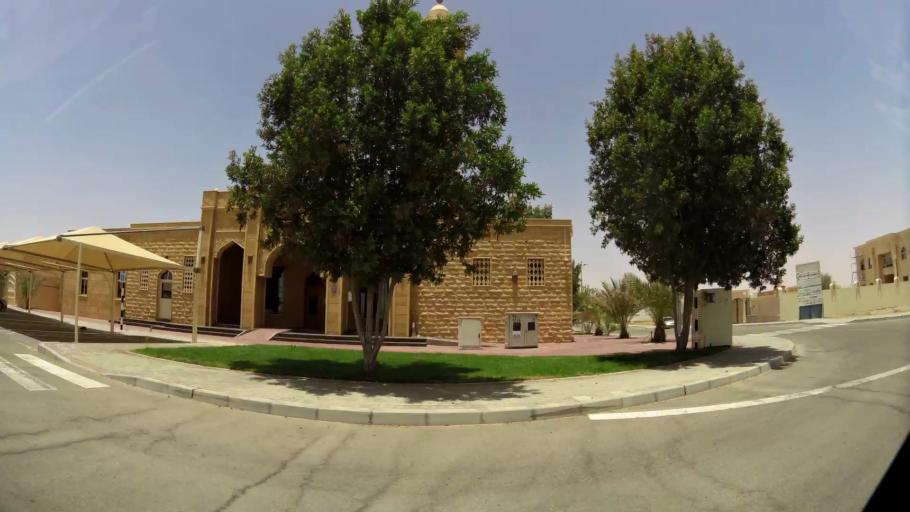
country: OM
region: Al Buraimi
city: Al Buraymi
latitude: 24.2927
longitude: 55.7416
